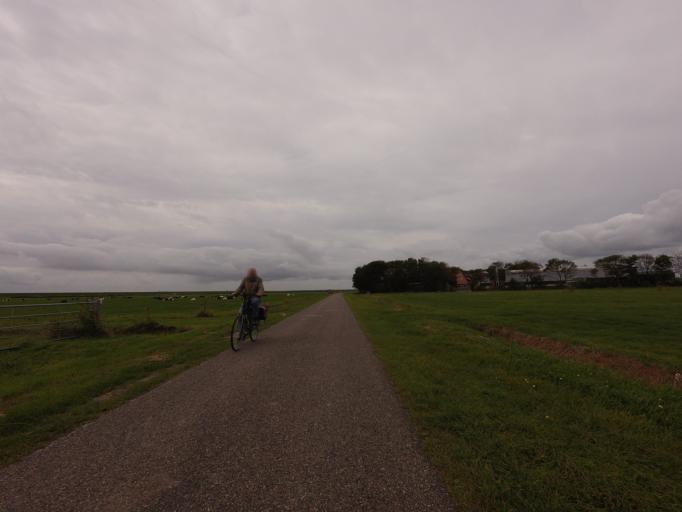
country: NL
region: Friesland
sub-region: Gemeente Ameland
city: Hollum
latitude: 53.4323
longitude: 5.6974
